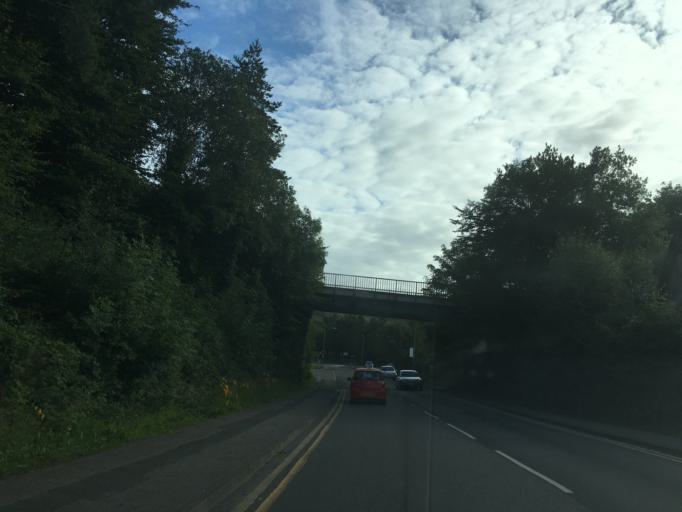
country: GB
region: Scotland
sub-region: Argyll and Bute
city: Oban
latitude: 56.4027
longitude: -5.4722
